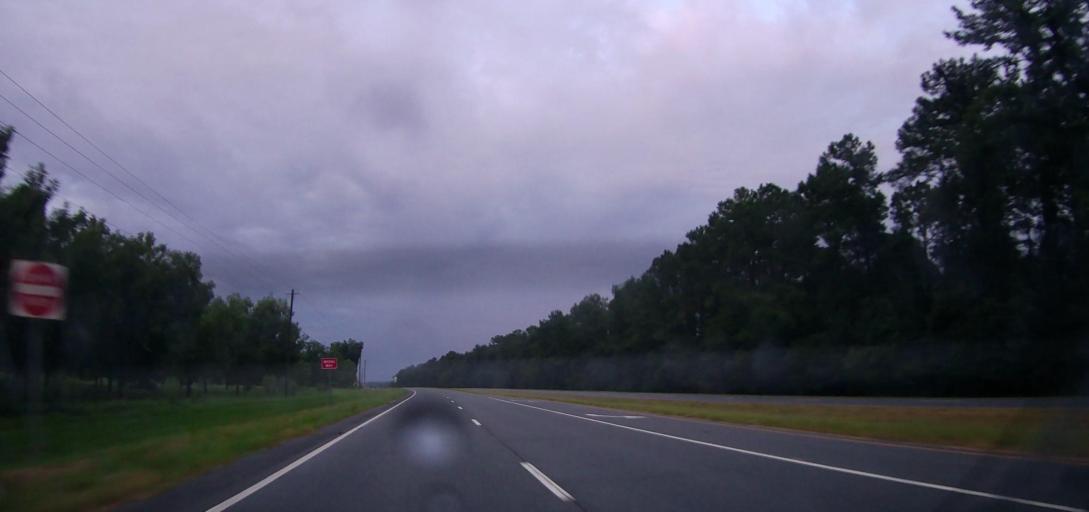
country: US
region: Georgia
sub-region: Lanier County
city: Lakeland
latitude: 30.9169
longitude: -83.0574
